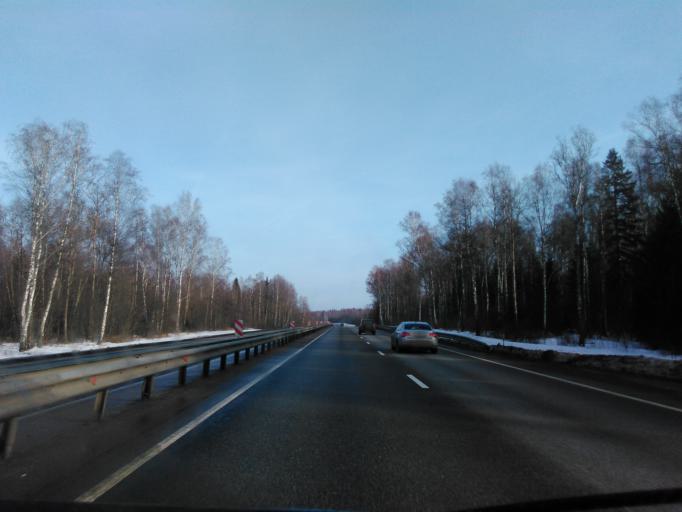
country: RU
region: Smolensk
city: Vyaz'ma
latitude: 55.1932
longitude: 33.9434
